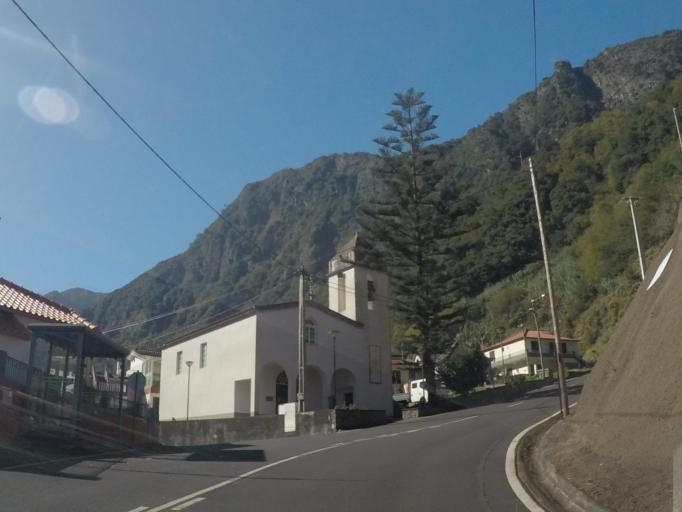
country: PT
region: Madeira
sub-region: Sao Vicente
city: Sao Vicente
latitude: 32.7969
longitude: -16.9691
